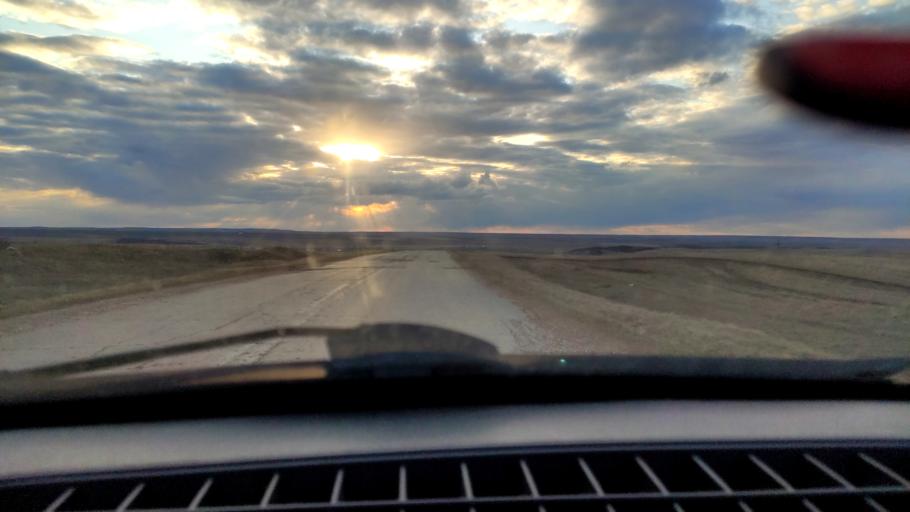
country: RU
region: Bashkortostan
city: Tolbazy
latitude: 54.0115
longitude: 55.5714
